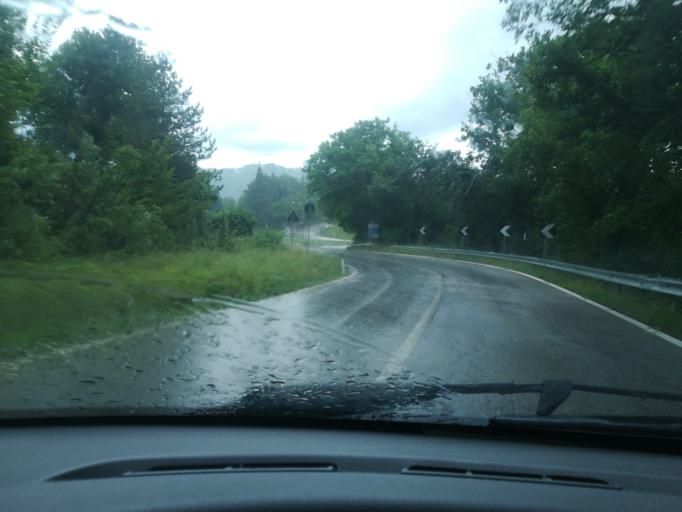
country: IT
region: The Marches
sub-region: Province of Fermo
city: Amandola
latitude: 42.9896
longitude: 13.3434
